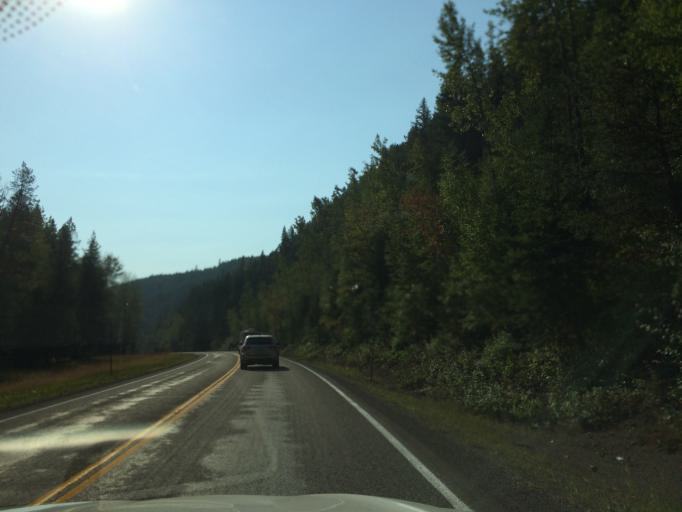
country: US
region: Montana
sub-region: Flathead County
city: Columbia Falls
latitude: 48.4915
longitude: -113.8789
